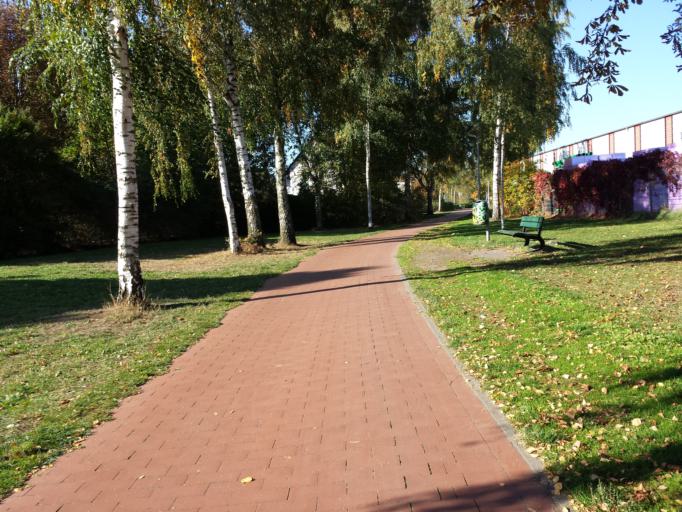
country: DE
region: Lower Saxony
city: Ritterhude
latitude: 53.1354
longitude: 8.7360
